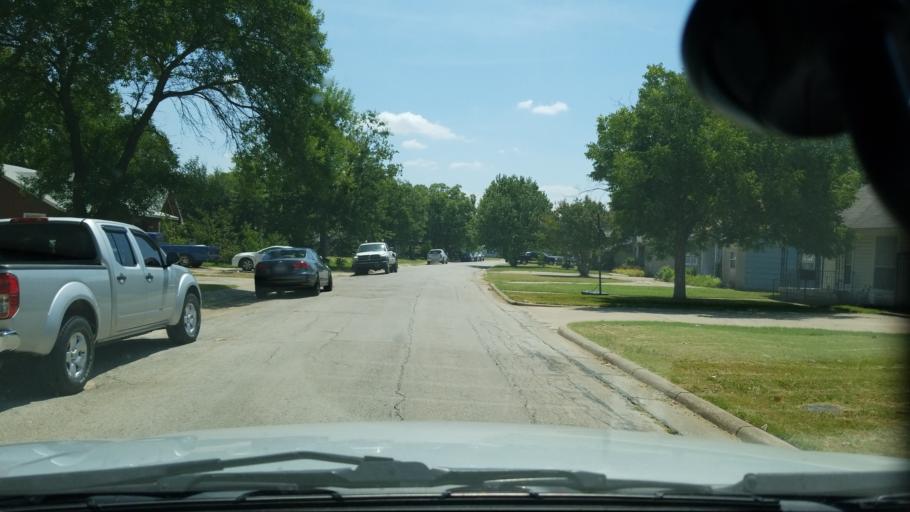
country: US
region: Texas
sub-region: Dallas County
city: Grand Prairie
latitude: 32.7508
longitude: -96.9572
